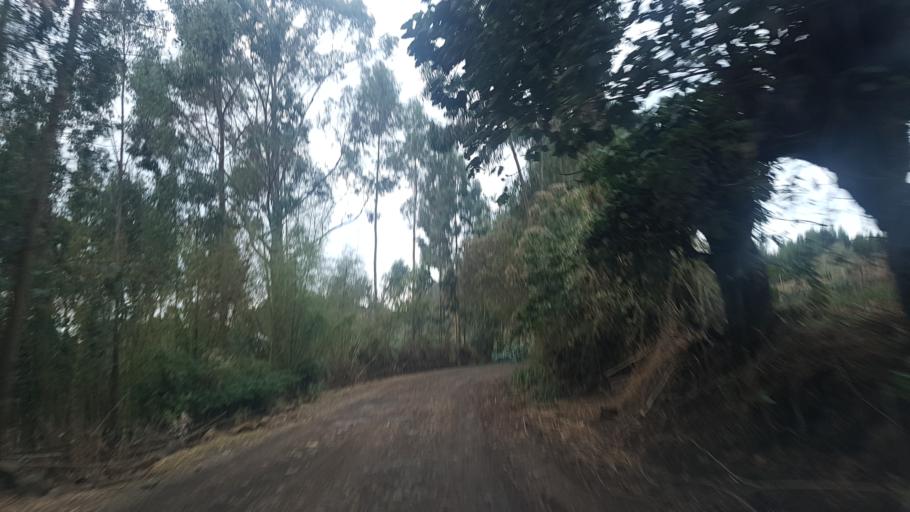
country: ET
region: Amhara
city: Finote Selam
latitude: 10.8008
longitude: 37.6635
